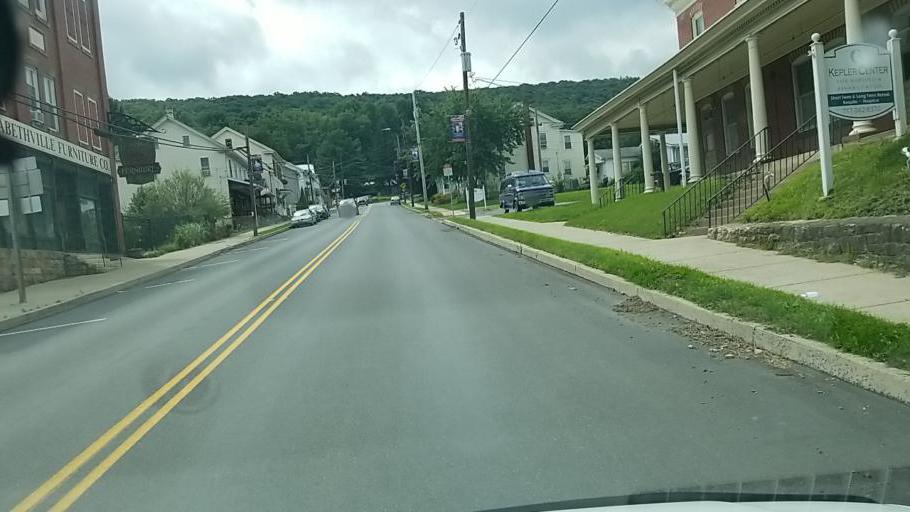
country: US
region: Pennsylvania
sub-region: Dauphin County
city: Elizabethville
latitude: 40.5478
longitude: -76.8115
